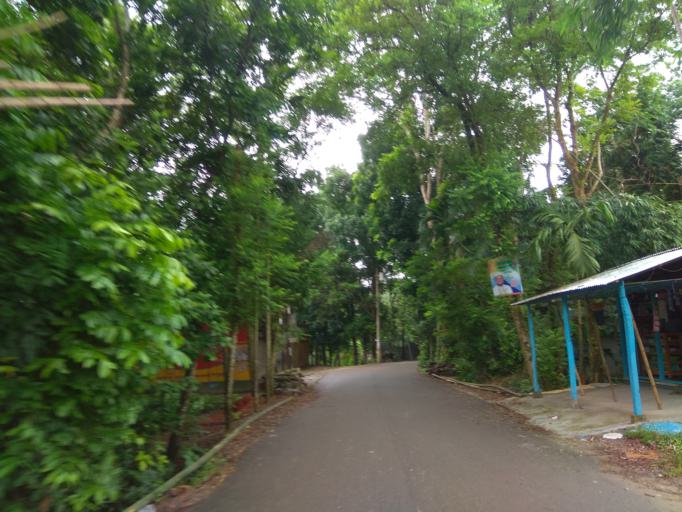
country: BD
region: Dhaka
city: Dohar
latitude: 23.4378
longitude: 90.0739
